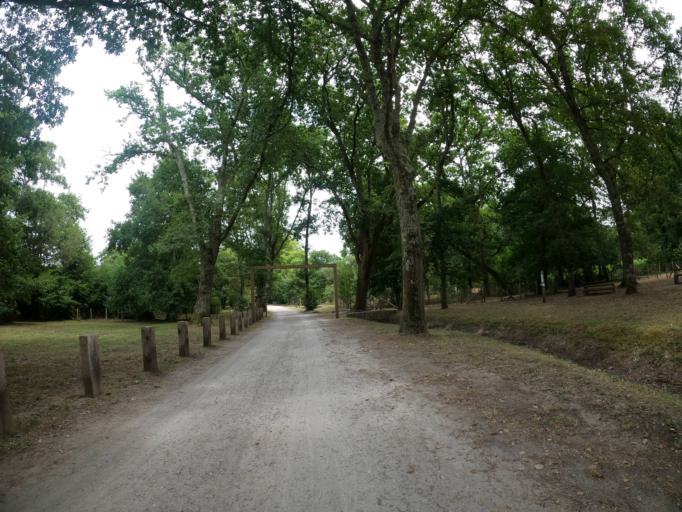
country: FR
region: Aquitaine
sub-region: Departement des Landes
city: Leon
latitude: 43.8871
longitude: -1.3140
